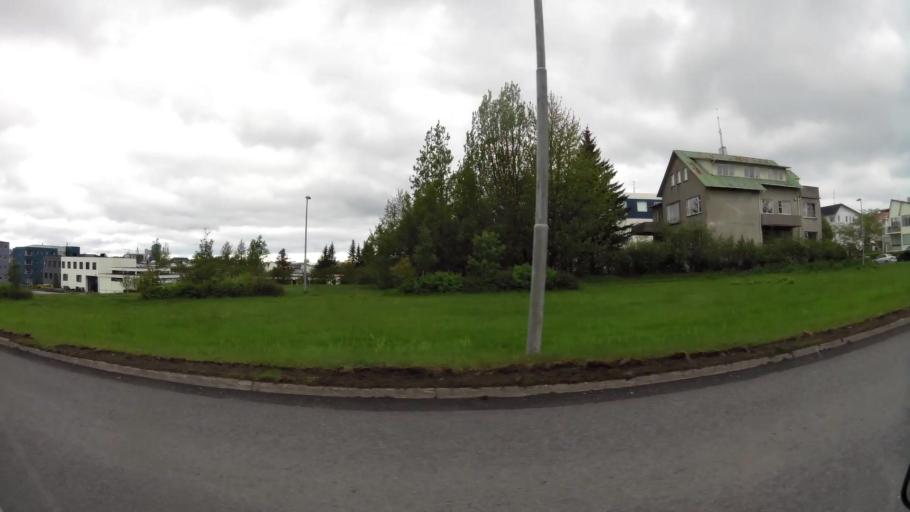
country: IS
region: Capital Region
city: Reykjavik
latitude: 64.1487
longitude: -21.8735
